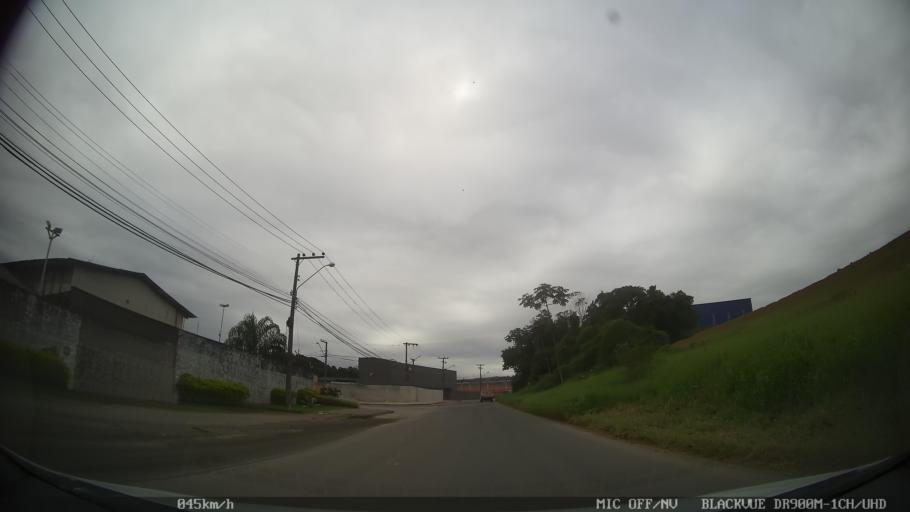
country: BR
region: Santa Catarina
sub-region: Joinville
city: Joinville
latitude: -26.2625
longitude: -48.8839
